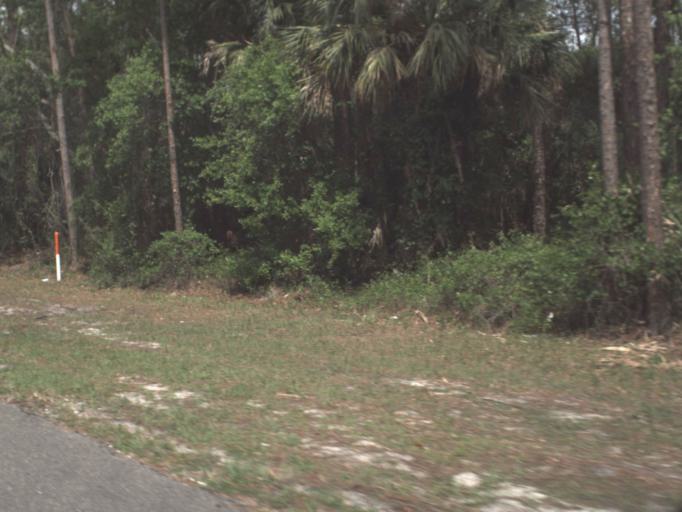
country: US
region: Florida
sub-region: Flagler County
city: Bunnell
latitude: 29.3887
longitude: -81.3089
